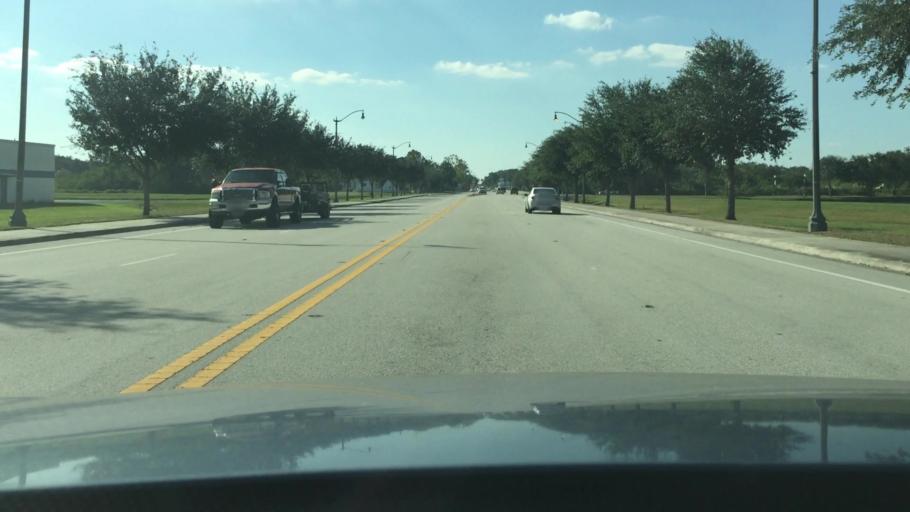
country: US
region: Florida
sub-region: Osceola County
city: Kissimmee
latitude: 28.2972
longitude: -81.4098
